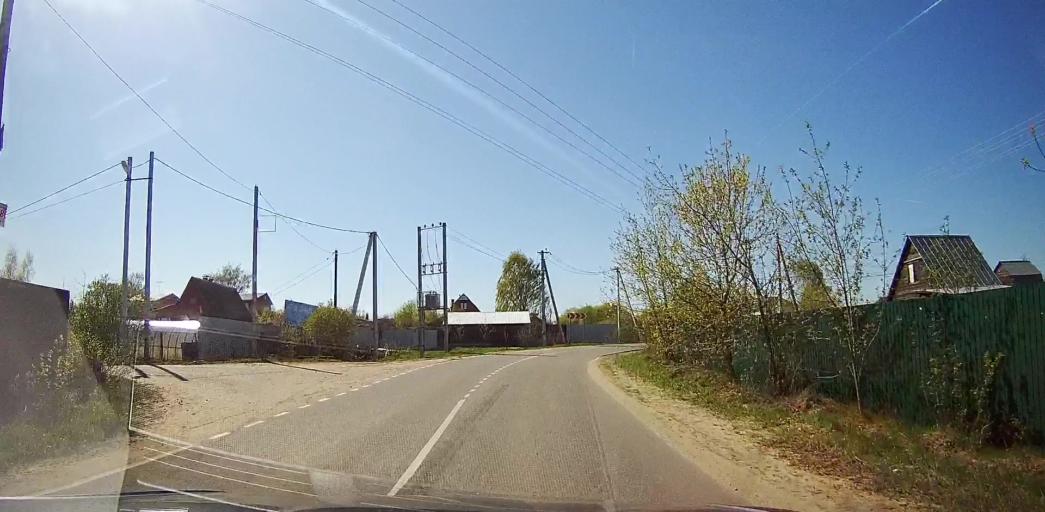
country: RU
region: Moskovskaya
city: Bronnitsy
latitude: 55.4727
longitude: 38.2602
